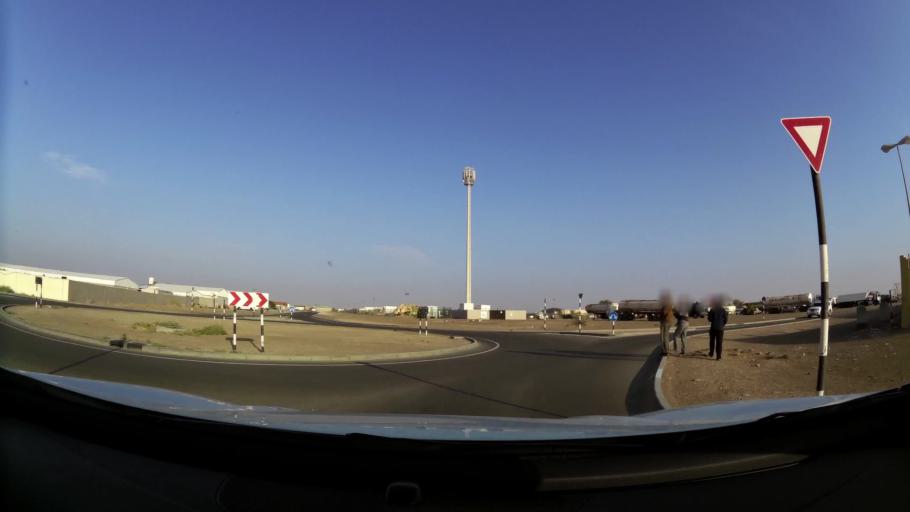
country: AE
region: Abu Dhabi
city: Al Ain
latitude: 24.1373
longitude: 55.8221
